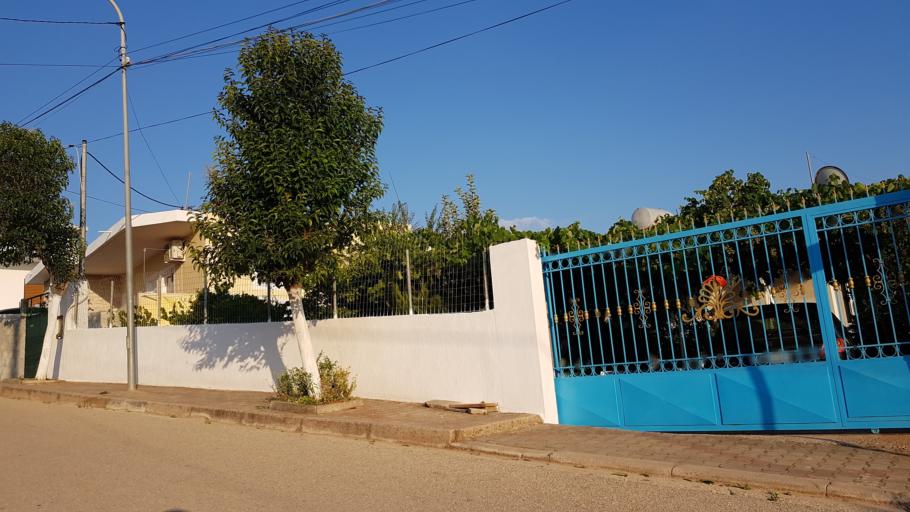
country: AL
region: Vlore
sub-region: Rrethi i Sarandes
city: Xarre
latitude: 39.7728
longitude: 20.0080
